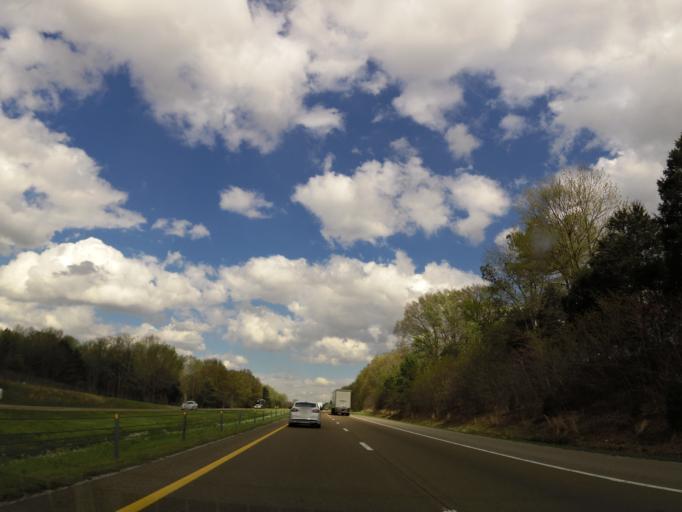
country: US
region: Tennessee
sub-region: Crockett County
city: Bells
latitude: 35.6131
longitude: -89.0122
